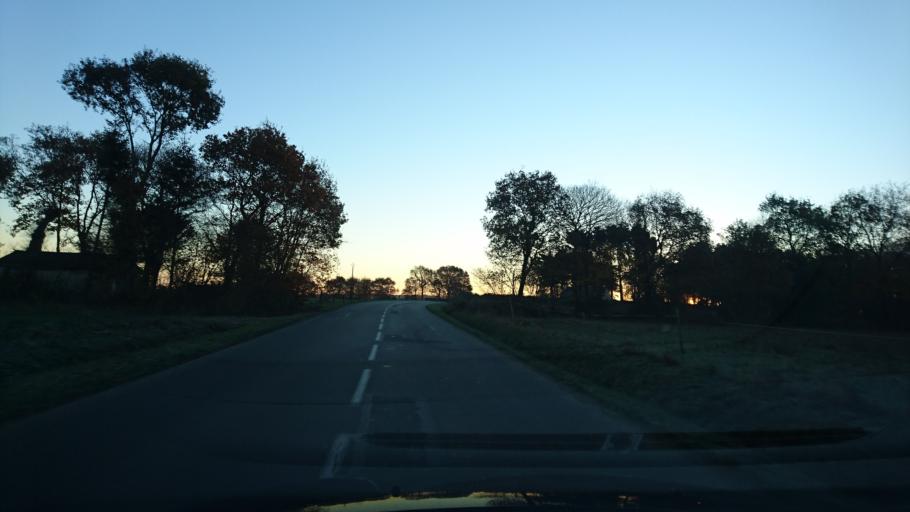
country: FR
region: Brittany
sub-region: Departement des Cotes-d'Armor
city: Saint-Julien
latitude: 48.4604
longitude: -2.7807
